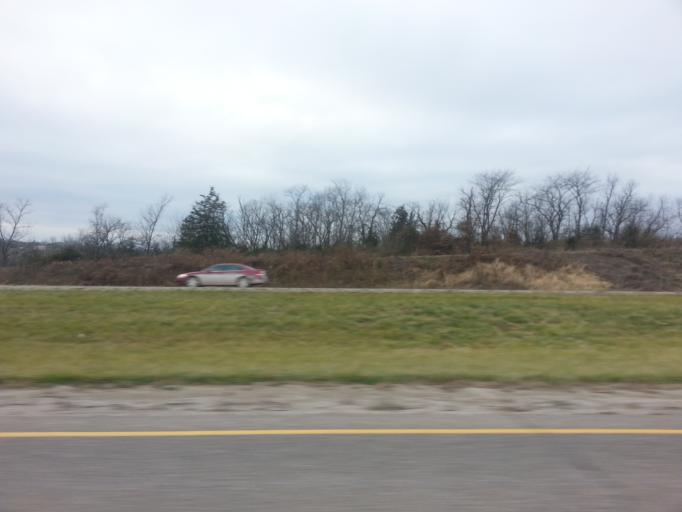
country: US
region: Iowa
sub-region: Henry County
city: Mount Pleasant
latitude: 40.9216
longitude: -91.5410
